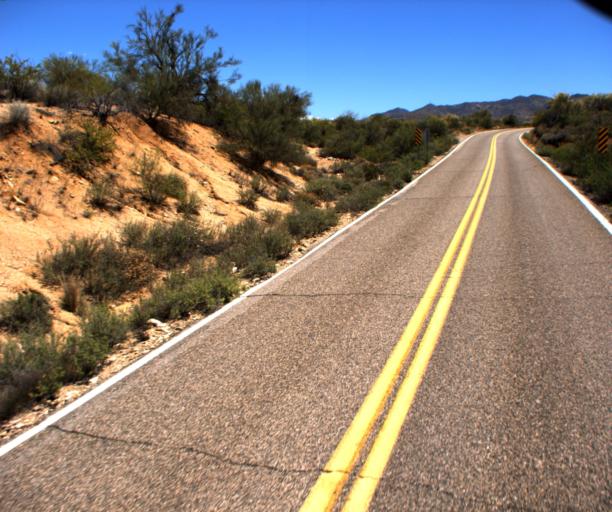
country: US
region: Arizona
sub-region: Yavapai County
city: Bagdad
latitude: 34.4700
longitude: -113.0513
